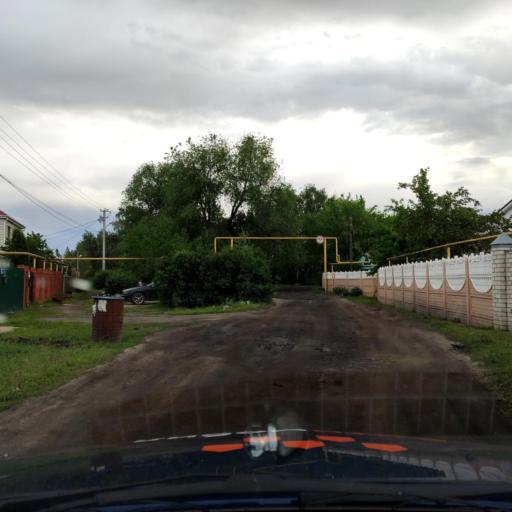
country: RU
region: Voronezj
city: Pridonskoy
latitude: 51.6752
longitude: 39.0745
